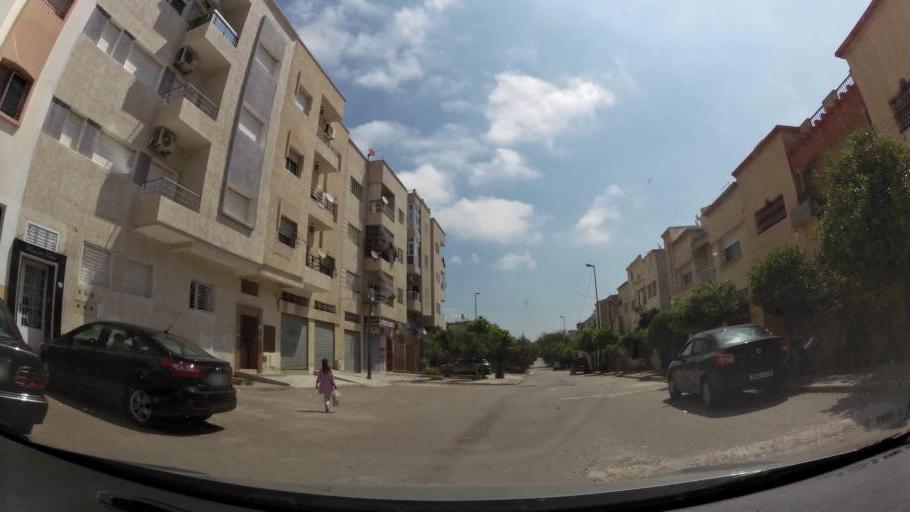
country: MA
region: Fes-Boulemane
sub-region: Fes
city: Fes
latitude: 34.0619
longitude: -5.0356
